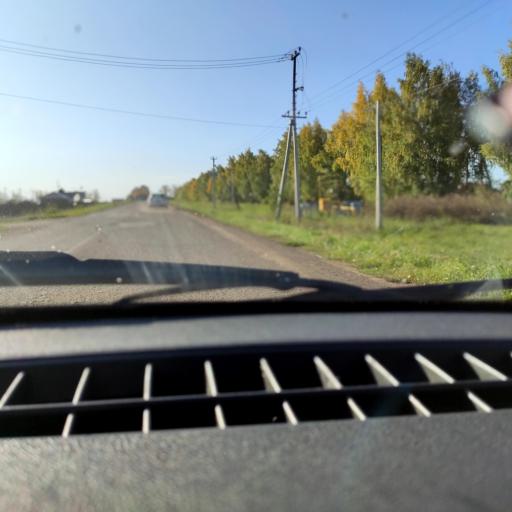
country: RU
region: Bashkortostan
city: Avdon
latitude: 54.5950
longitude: 55.7999
